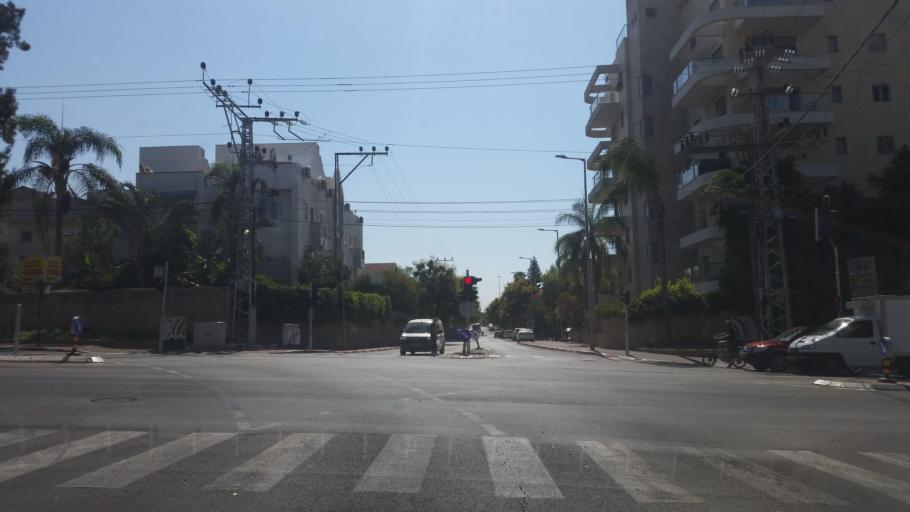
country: IL
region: Central District
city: Ra'anana
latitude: 32.1785
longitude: 34.8845
